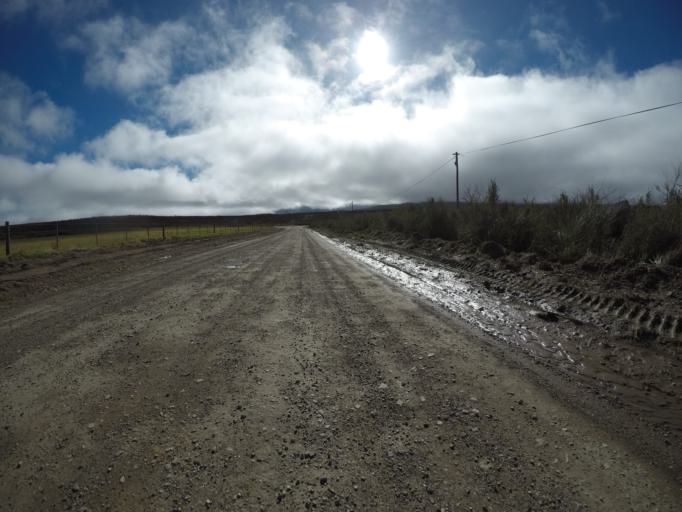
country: ZA
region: Western Cape
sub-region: Cape Winelands District Municipality
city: Ashton
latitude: -34.1230
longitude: 19.8390
